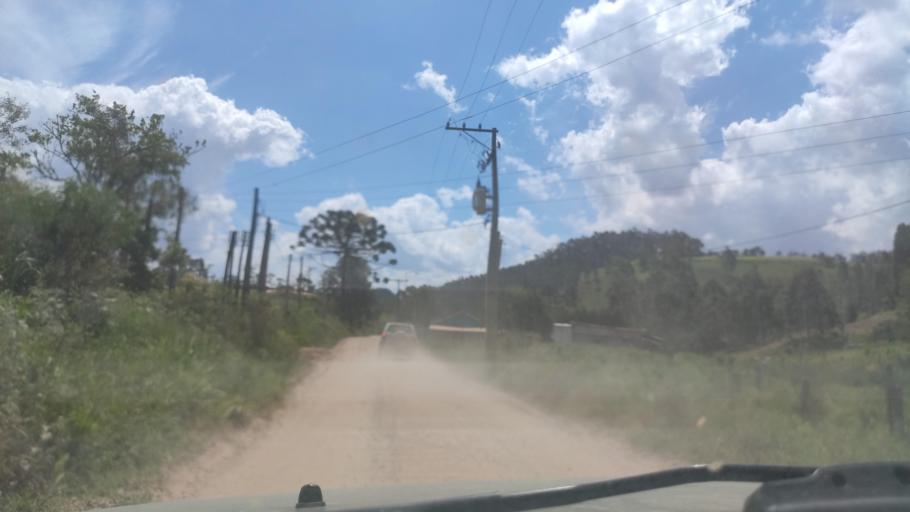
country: BR
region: Minas Gerais
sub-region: Cambui
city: Cambui
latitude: -22.7071
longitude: -46.0245
